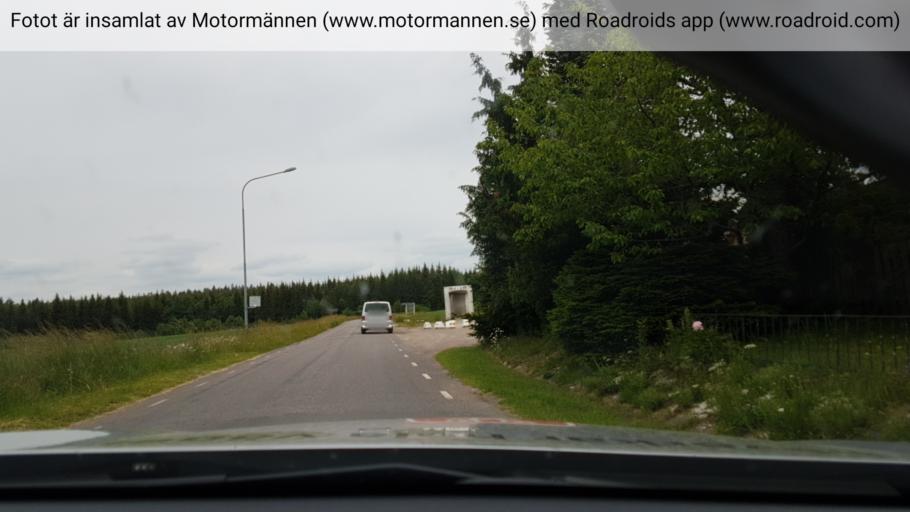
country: SE
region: Vaestra Goetaland
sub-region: Tidaholms Kommun
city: Tidaholm
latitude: 58.0701
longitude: 13.9454
